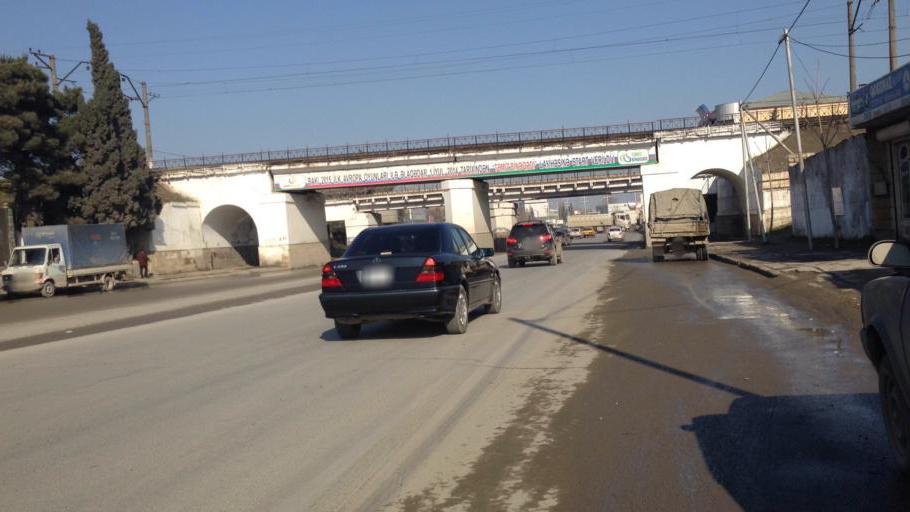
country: AZ
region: Baki
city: Binagadi
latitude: 40.4390
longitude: 49.8448
